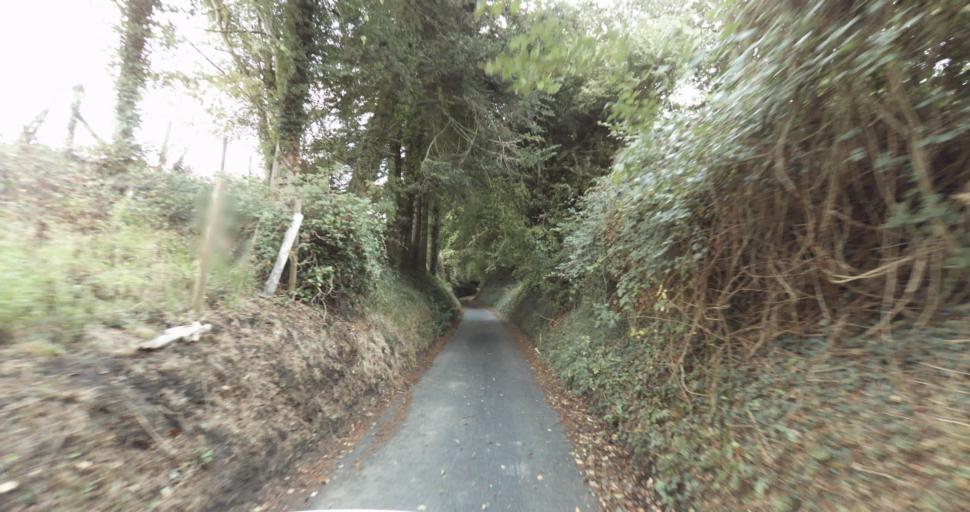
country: FR
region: Lower Normandy
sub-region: Departement de l'Orne
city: Vimoutiers
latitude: 48.9140
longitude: 0.1091
